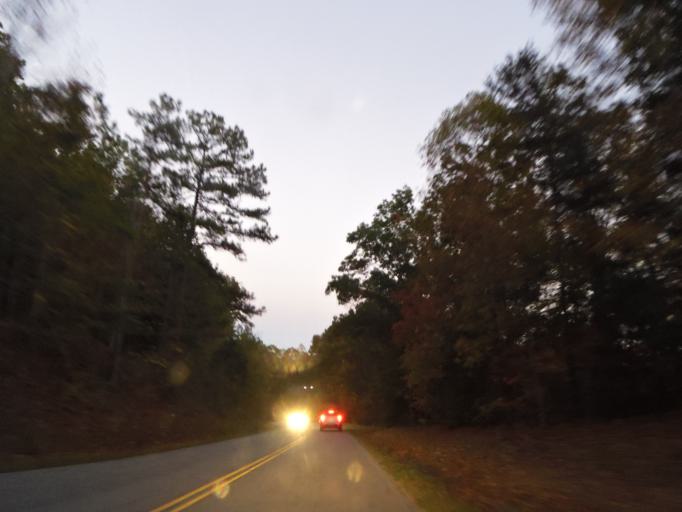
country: US
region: Tennessee
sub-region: Blount County
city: Wildwood
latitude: 35.7171
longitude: -83.8352
